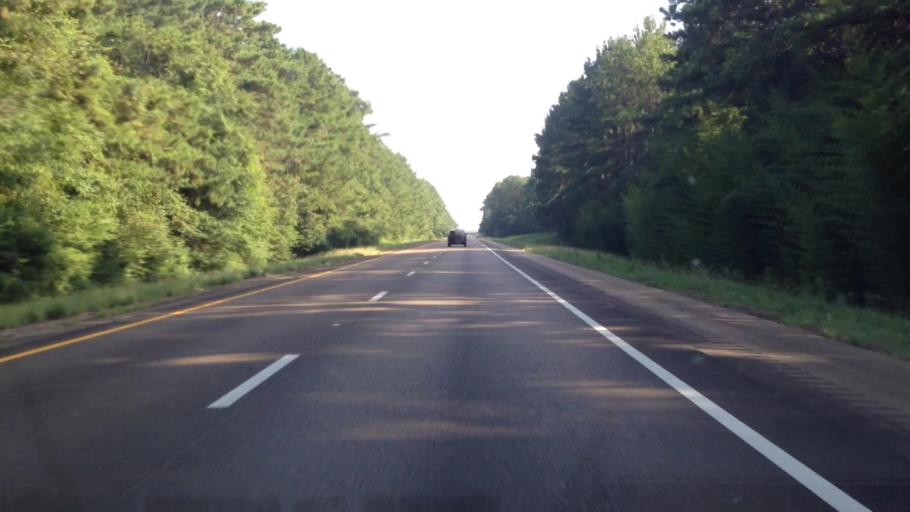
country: US
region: Mississippi
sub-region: Pike County
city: Summit
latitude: 31.3397
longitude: -90.4777
